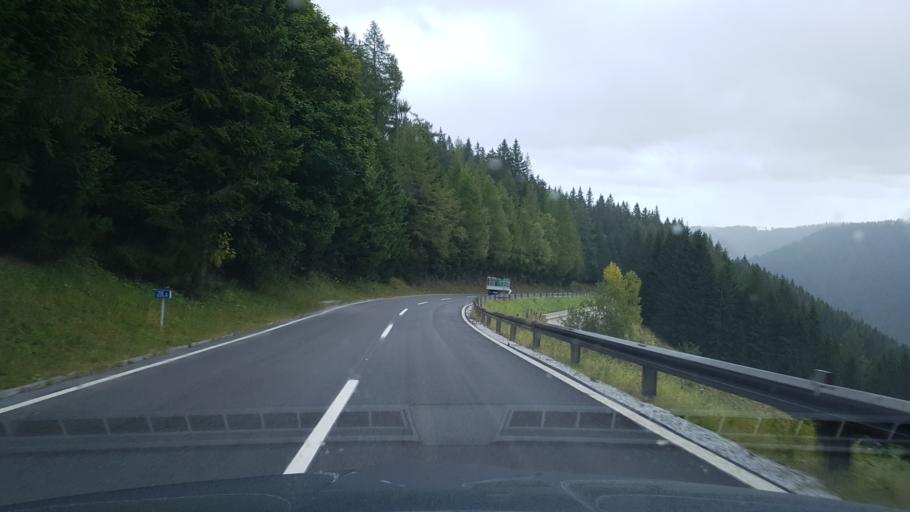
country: AT
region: Styria
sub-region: Politischer Bezirk Voitsberg
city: Salla
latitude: 47.1144
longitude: 14.9295
